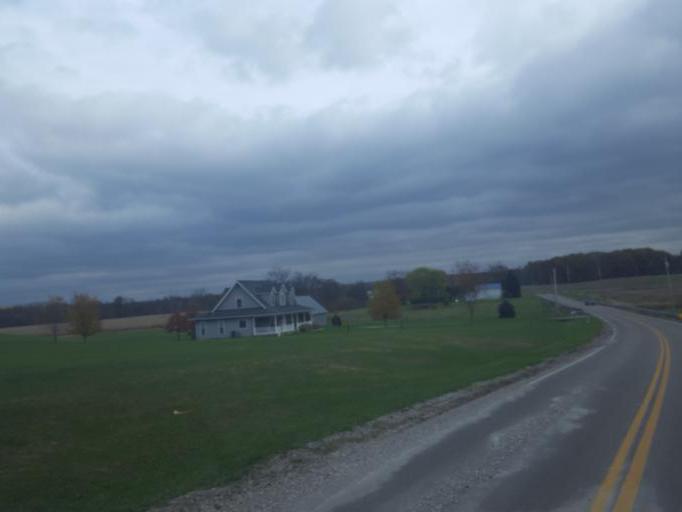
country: US
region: Ohio
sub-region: Crawford County
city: Galion
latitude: 40.7045
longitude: -82.7108
